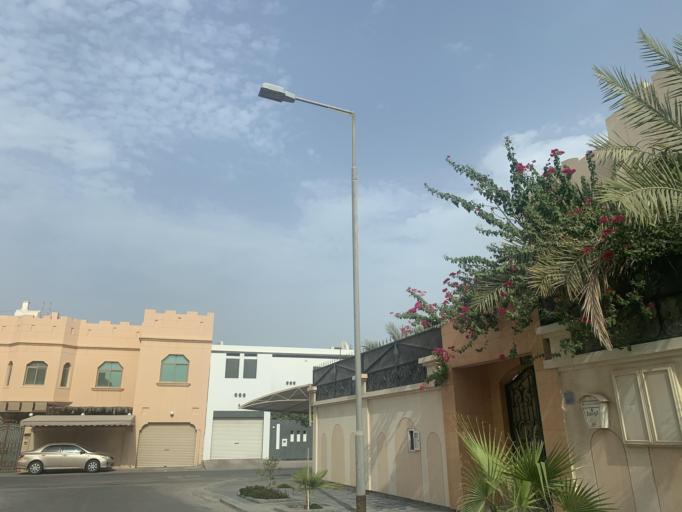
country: BH
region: Northern
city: Madinat `Isa
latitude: 26.1880
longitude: 50.4868
